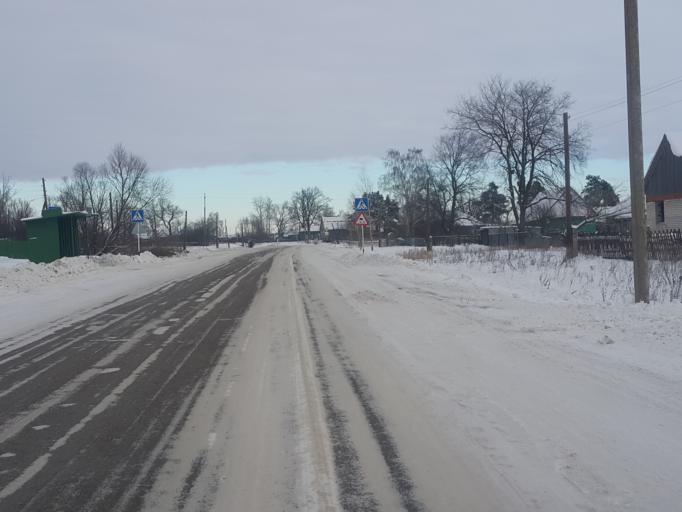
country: RU
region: Tambov
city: Platonovka
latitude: 52.8789
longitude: 41.8764
